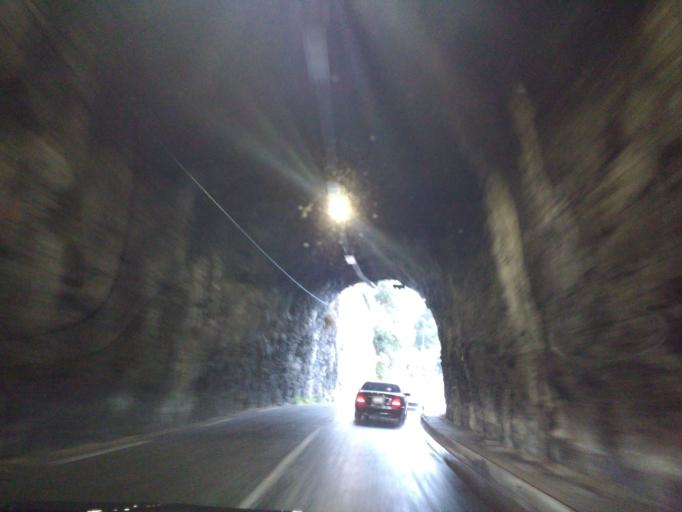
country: FR
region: Provence-Alpes-Cote d'Azur
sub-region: Departement des Alpes-Maritimes
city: Cap-d'Ail
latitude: 43.7238
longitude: 7.3907
